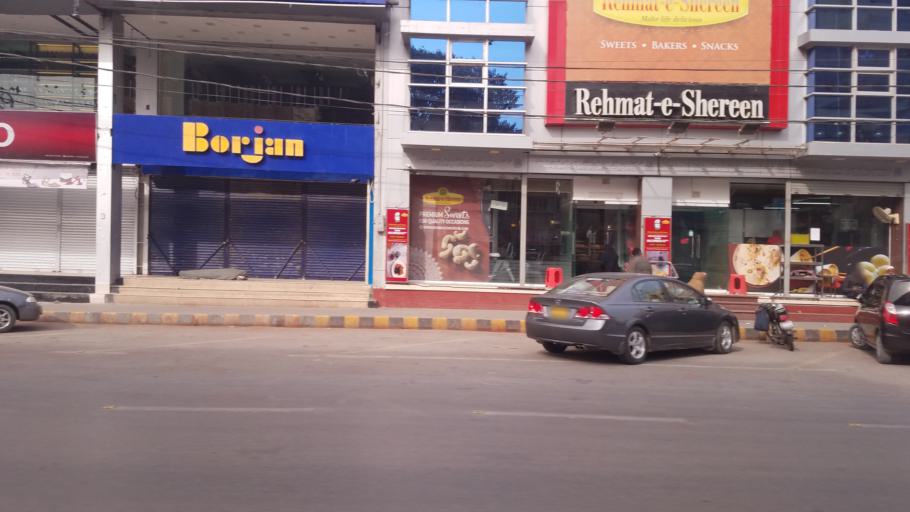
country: PK
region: Sindh
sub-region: Karachi District
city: Karachi
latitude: 24.8682
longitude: 67.0576
